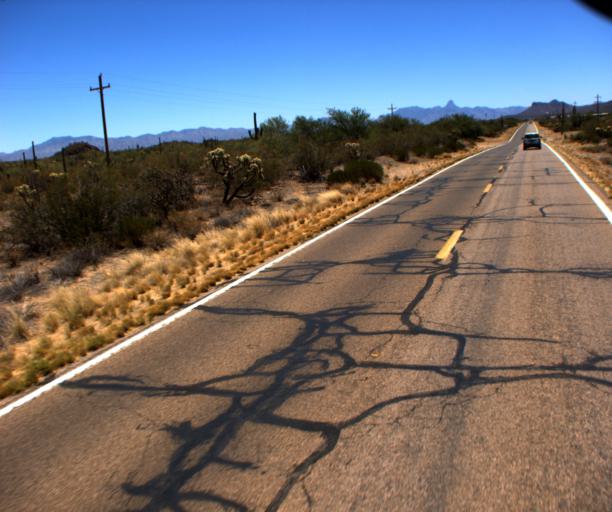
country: US
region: Arizona
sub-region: Pima County
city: Sells
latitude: 31.9428
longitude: -111.9254
